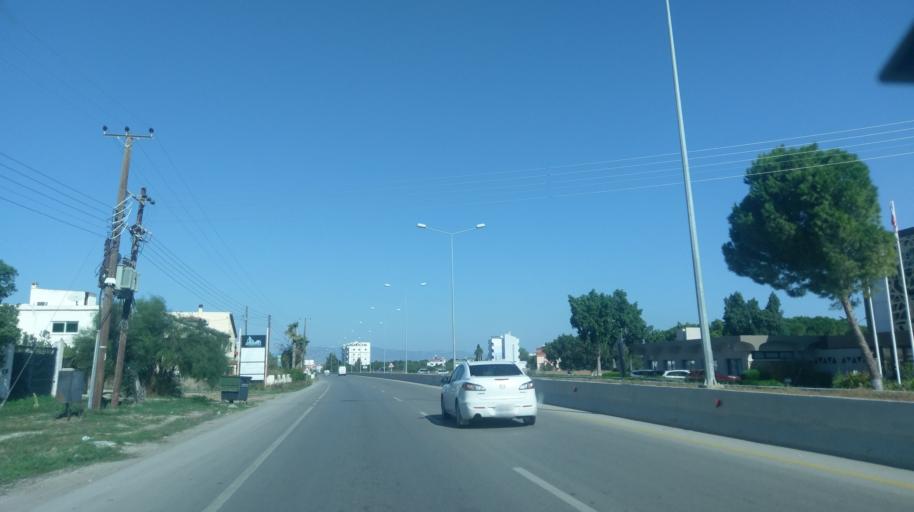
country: CY
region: Ammochostos
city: Famagusta
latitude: 35.1871
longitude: 33.8943
